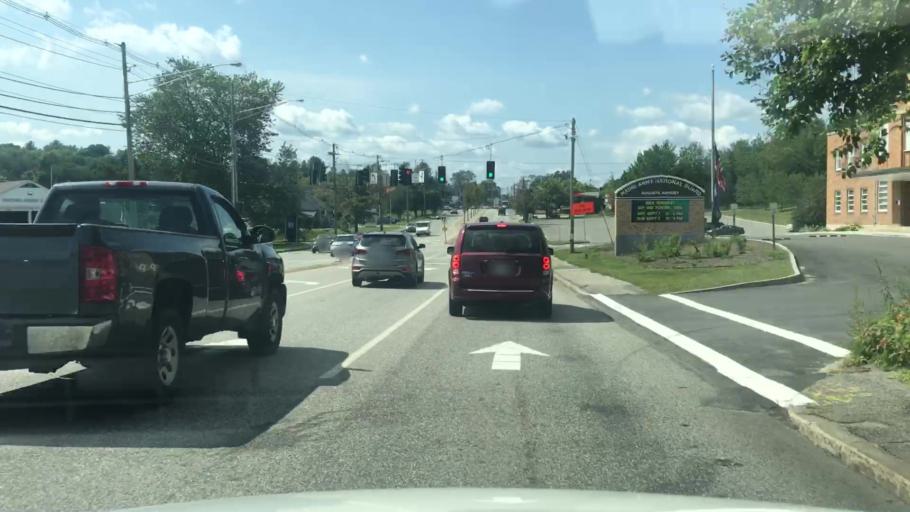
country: US
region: Maine
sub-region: Kennebec County
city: Augusta
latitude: 44.3133
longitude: -69.7957
